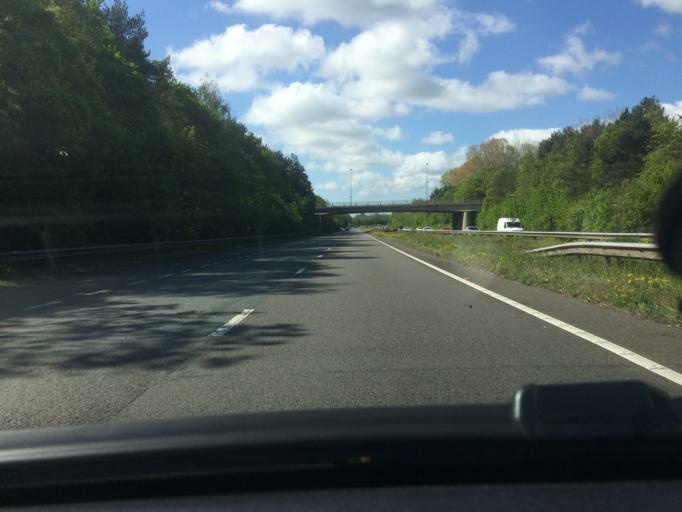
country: GB
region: England
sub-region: Cheshire West and Chester
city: Hoole
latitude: 53.1739
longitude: -2.8608
